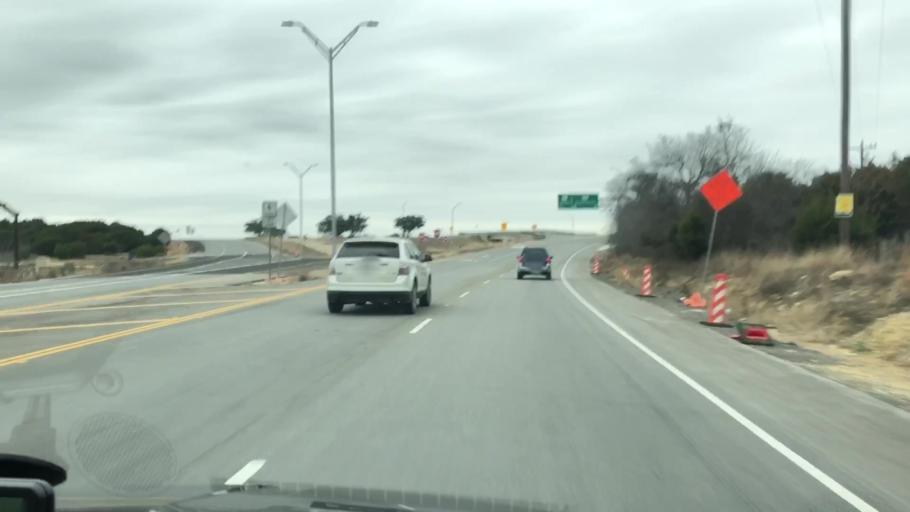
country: US
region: Texas
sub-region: Hamilton County
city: Hico
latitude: 32.0296
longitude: -98.0803
